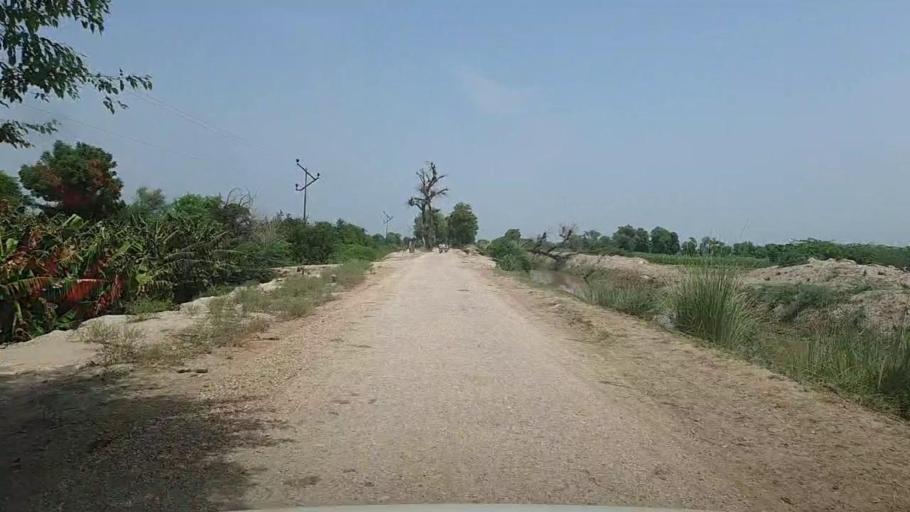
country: PK
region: Sindh
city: Karaundi
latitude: 26.9087
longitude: 68.3338
